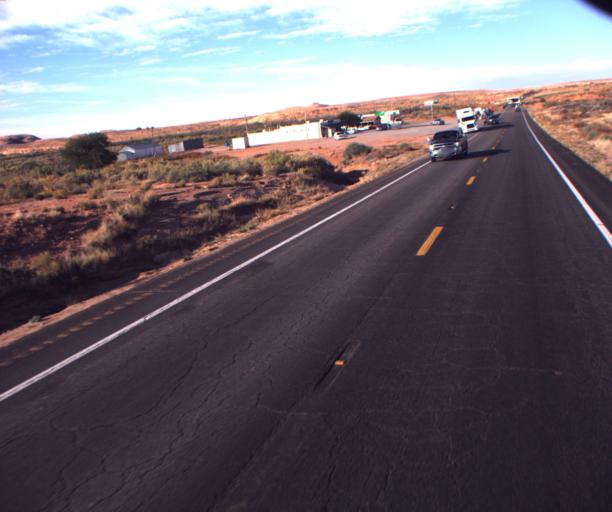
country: US
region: Arizona
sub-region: Apache County
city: Many Farms
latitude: 36.9245
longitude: -109.6009
